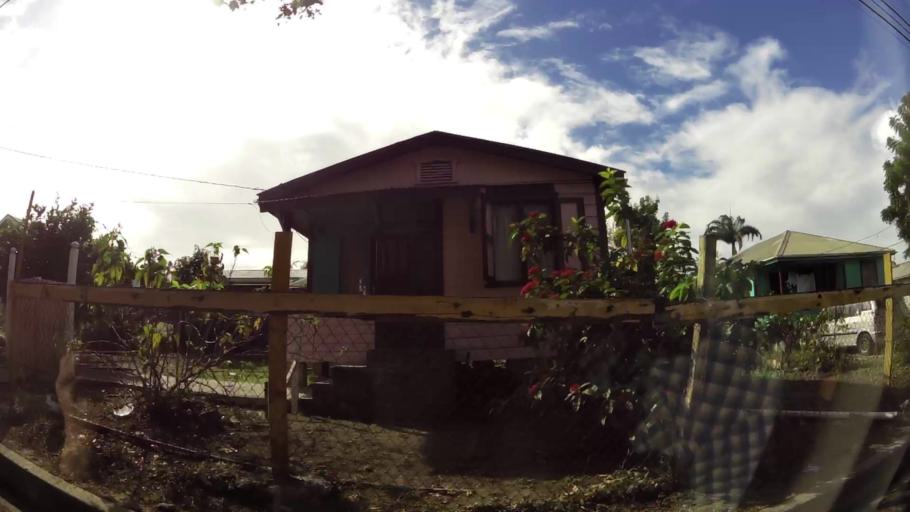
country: AG
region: Saint John
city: Saint John's
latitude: 17.1212
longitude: -61.8280
